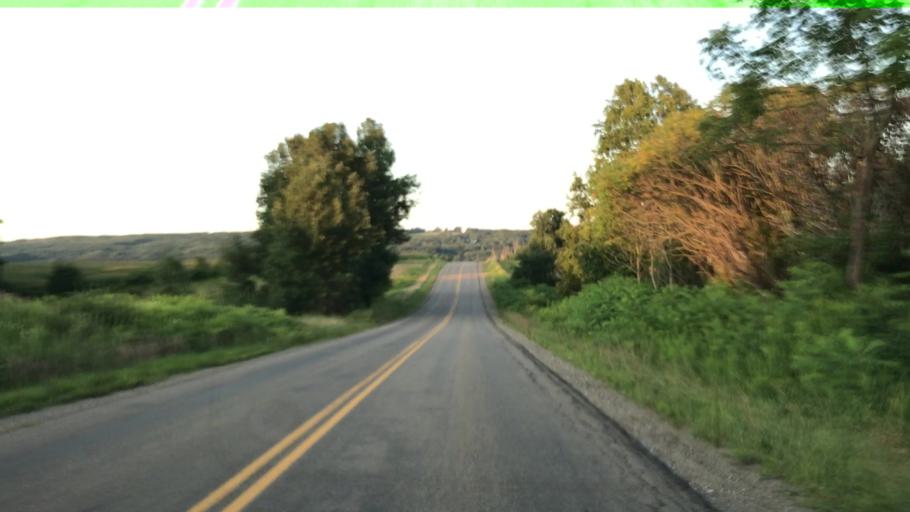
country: US
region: New York
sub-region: Chautauqua County
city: Brocton
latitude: 42.3107
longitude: -79.3736
